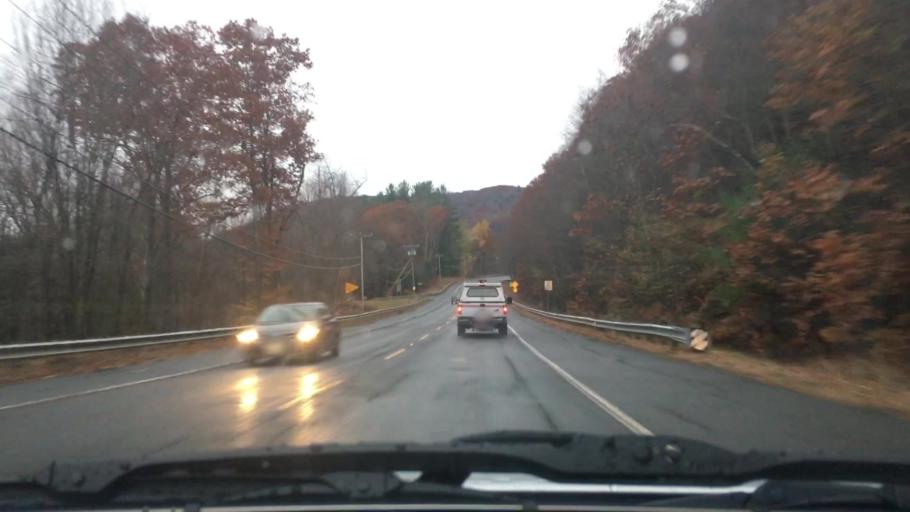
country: US
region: Massachusetts
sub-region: Hampden County
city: Westfield
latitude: 42.1724
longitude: -72.8323
